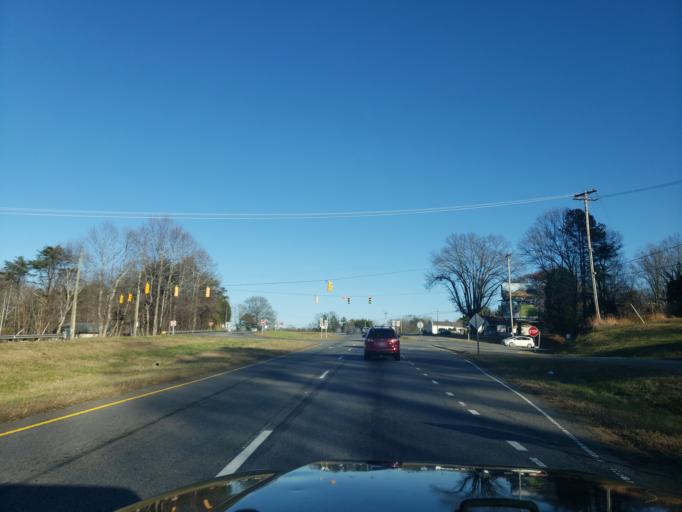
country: US
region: North Carolina
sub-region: Gaston County
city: Bessemer City
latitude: 35.2485
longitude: -81.2876
